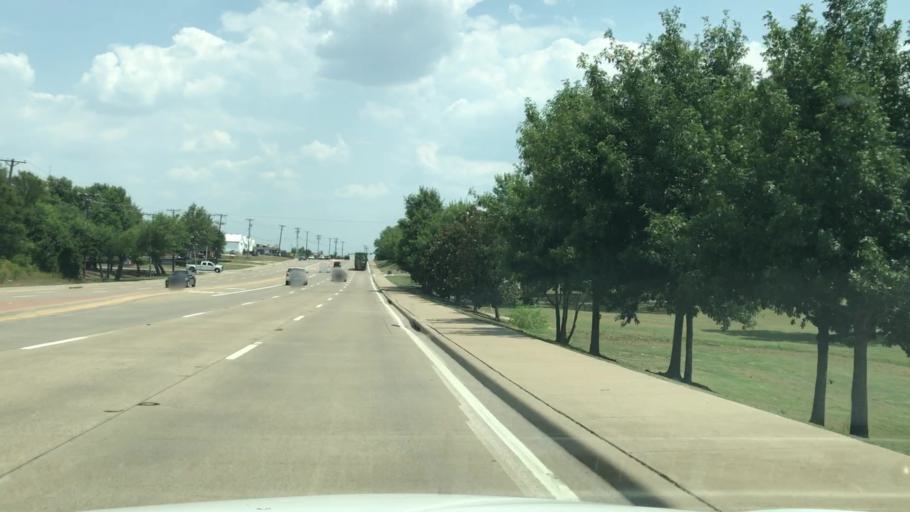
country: US
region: Texas
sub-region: Rockwall County
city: Rockwall
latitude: 32.9164
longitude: -96.4563
